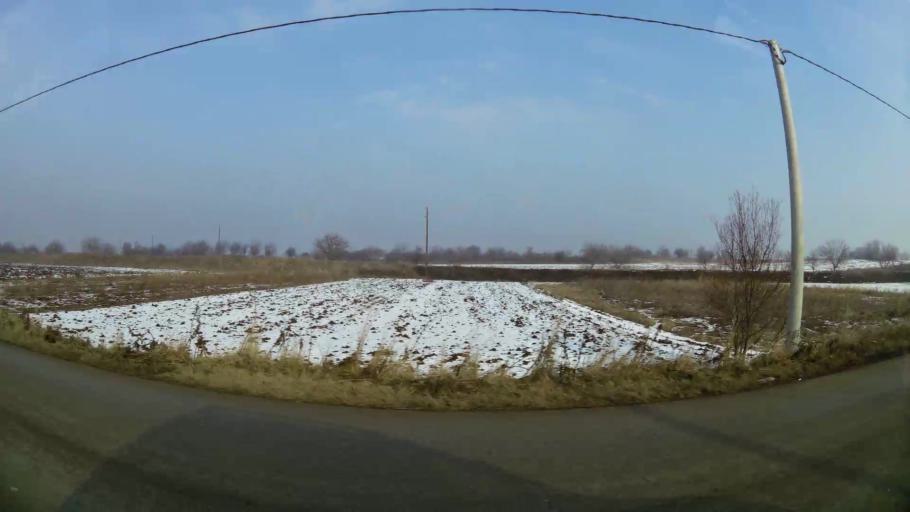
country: MK
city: Kadino
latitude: 41.9754
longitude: 21.6032
